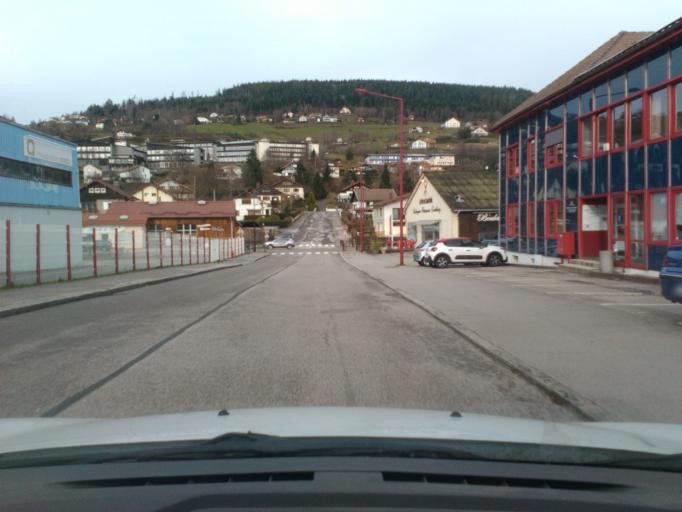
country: FR
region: Lorraine
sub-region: Departement des Vosges
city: Gerardmer
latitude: 48.0752
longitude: 6.8767
